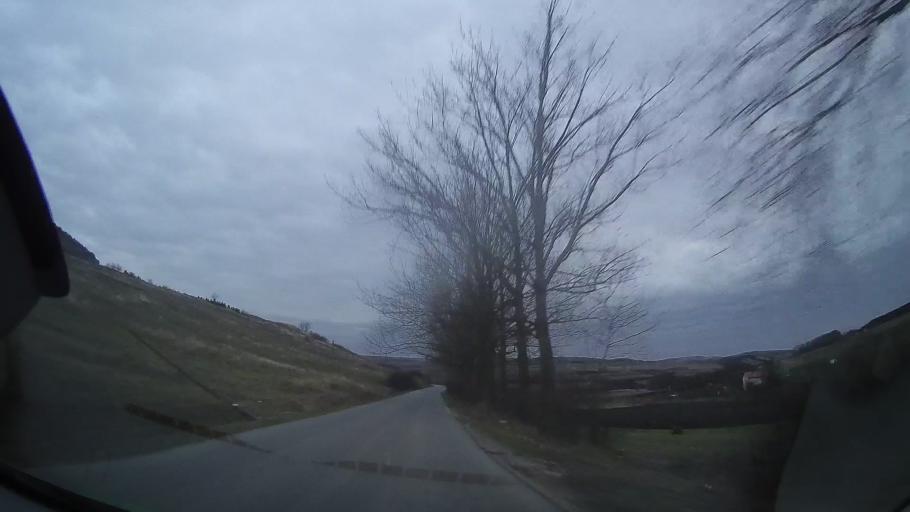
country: RO
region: Cluj
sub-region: Comuna Caianu
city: Caianu
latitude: 46.8064
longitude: 23.9298
